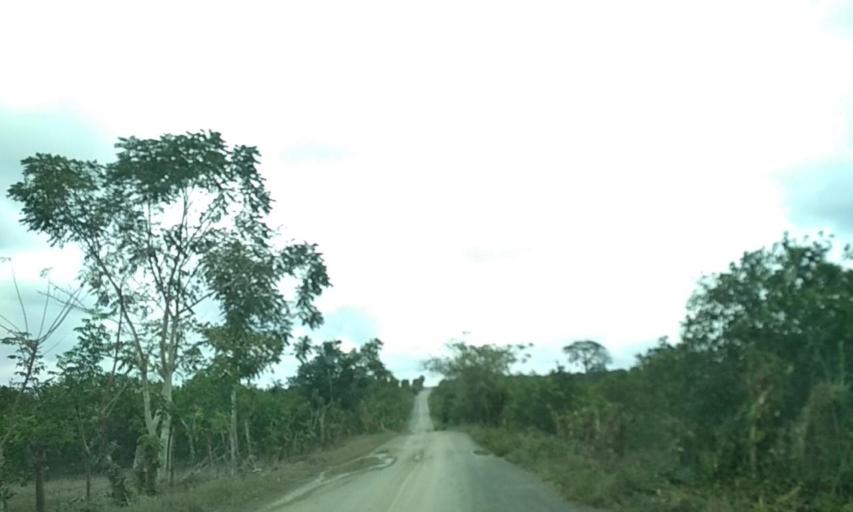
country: MX
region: Veracruz
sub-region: Papantla
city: El Chote
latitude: 20.3407
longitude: -97.3935
